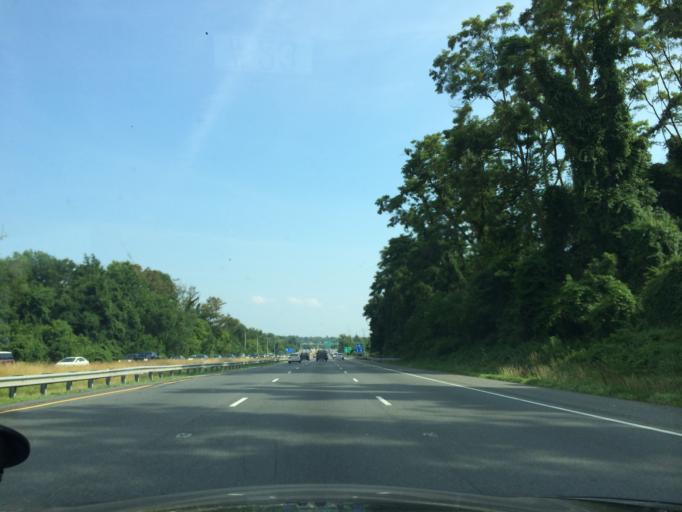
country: US
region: Maryland
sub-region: Howard County
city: Ellicott City
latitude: 39.2853
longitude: -76.8244
